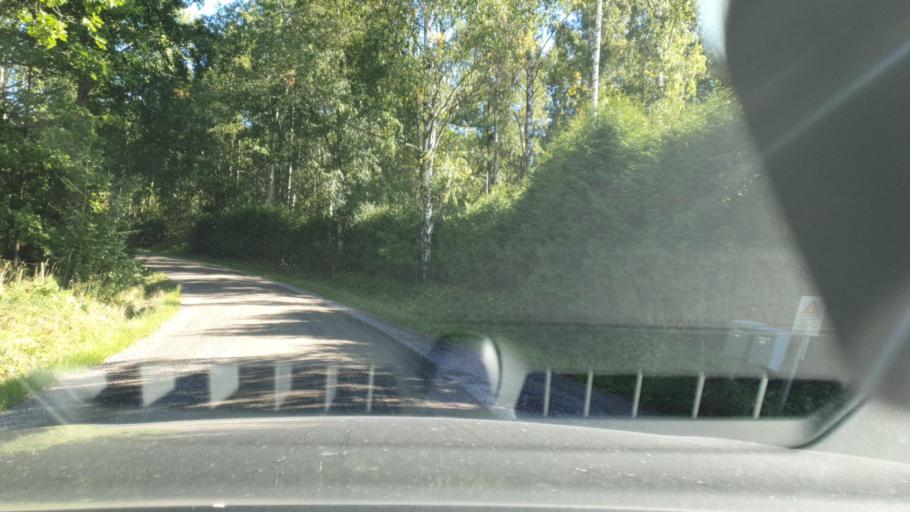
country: SE
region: OErebro
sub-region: Karlskoga Kommun
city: Karlskoga
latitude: 59.4402
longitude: 14.4176
